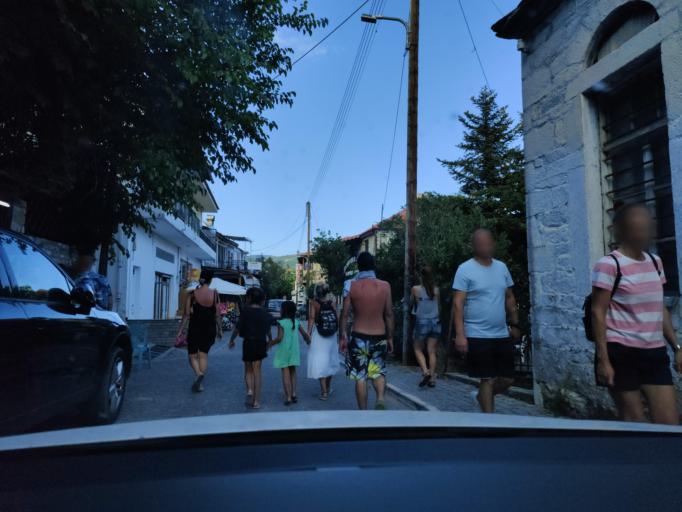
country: GR
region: East Macedonia and Thrace
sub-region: Nomos Kavalas
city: Potamia
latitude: 40.6595
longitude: 24.6928
